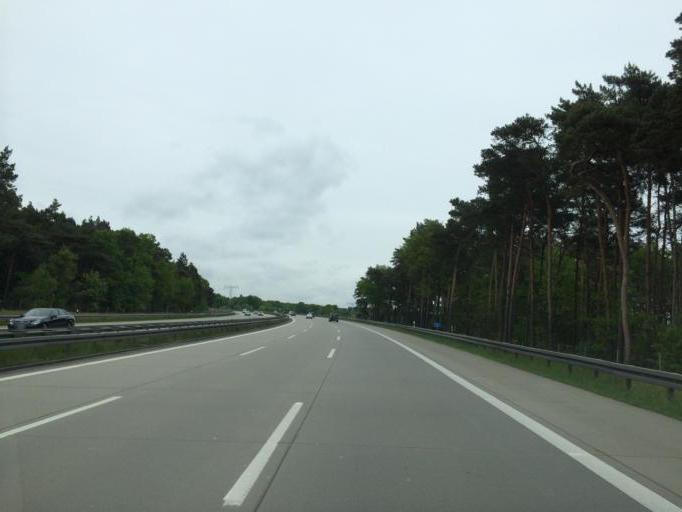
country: DE
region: Berlin
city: Wannsee
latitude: 52.3362
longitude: 13.1325
